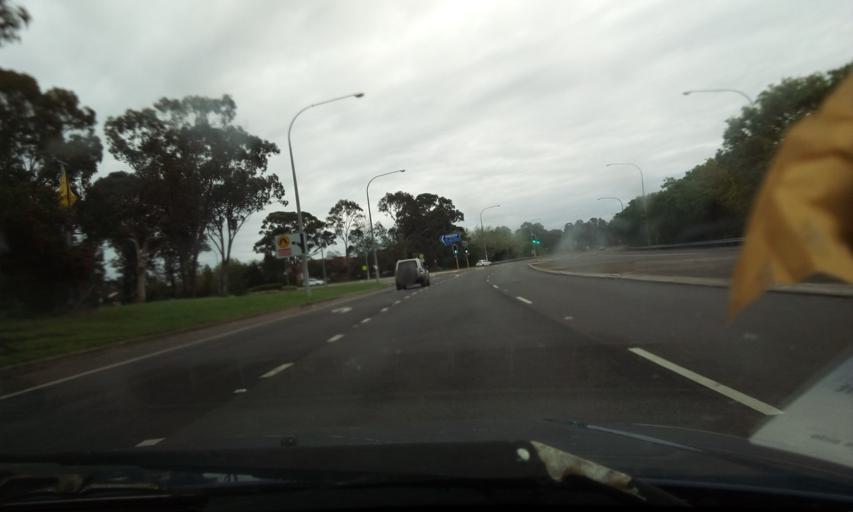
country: AU
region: New South Wales
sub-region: Camden
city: Camden South
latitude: -34.0749
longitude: 150.6957
